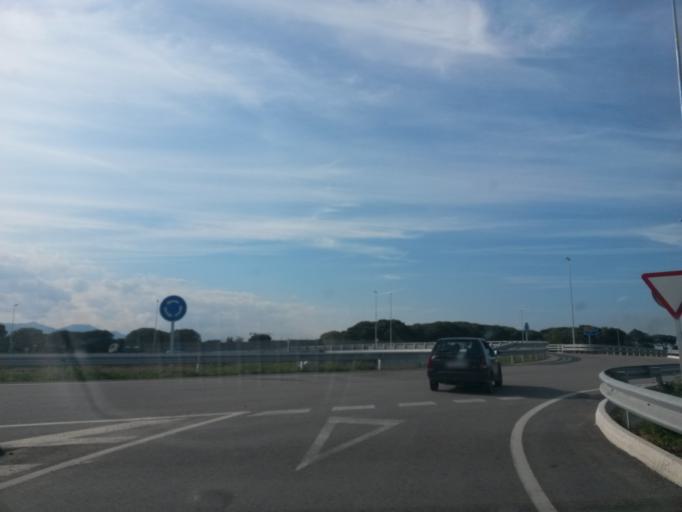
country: ES
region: Catalonia
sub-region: Provincia de Girona
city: Vilobi d'Onyar
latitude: 41.8510
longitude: 2.7729
